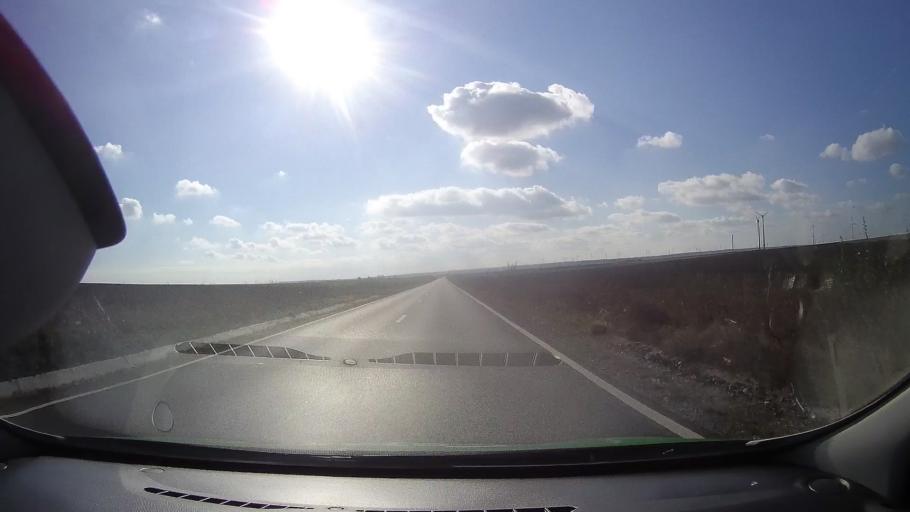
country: RO
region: Constanta
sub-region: Comuna Mihai Viteazu
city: Mihai Viteazu
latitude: 44.6736
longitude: 28.6846
